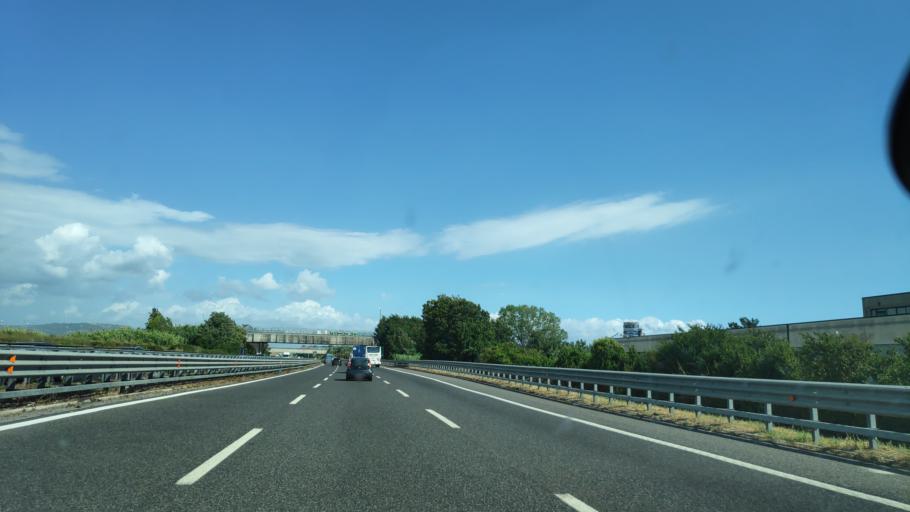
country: IT
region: Campania
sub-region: Provincia di Salerno
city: Sant'Antonio
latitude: 40.6384
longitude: 14.9050
